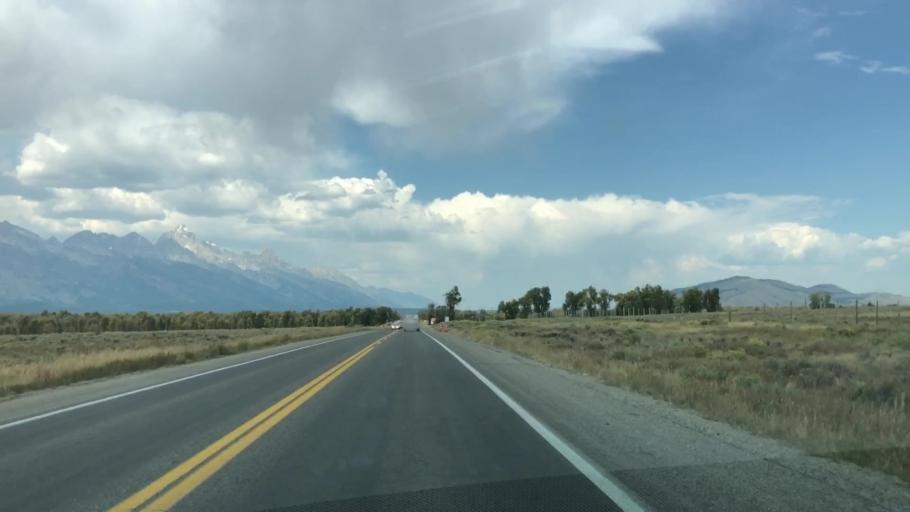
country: US
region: Wyoming
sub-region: Teton County
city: Jackson
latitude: 43.5567
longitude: -110.7326
